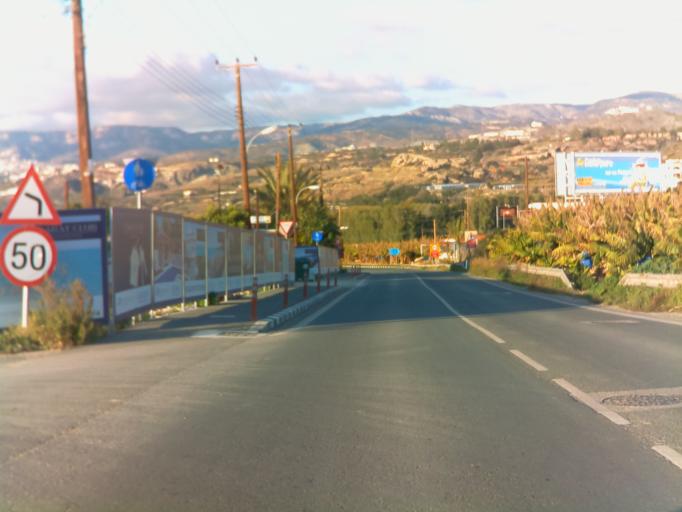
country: CY
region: Pafos
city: Kissonerga
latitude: 34.8304
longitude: 32.3925
